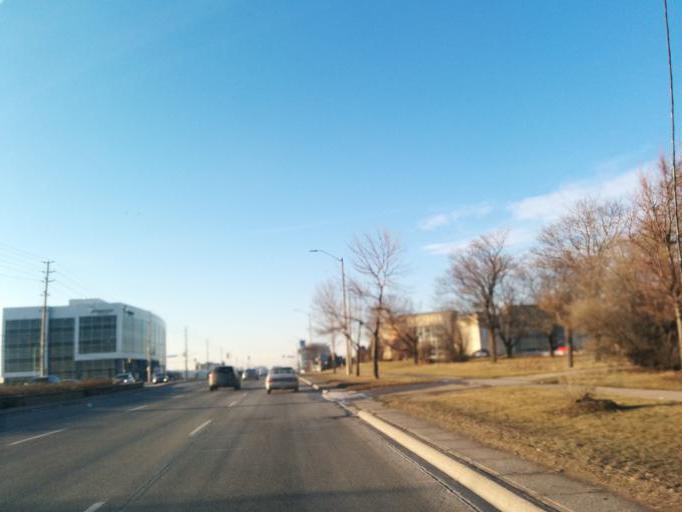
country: CA
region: Ontario
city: Mississauga
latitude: 43.6342
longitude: -79.6899
